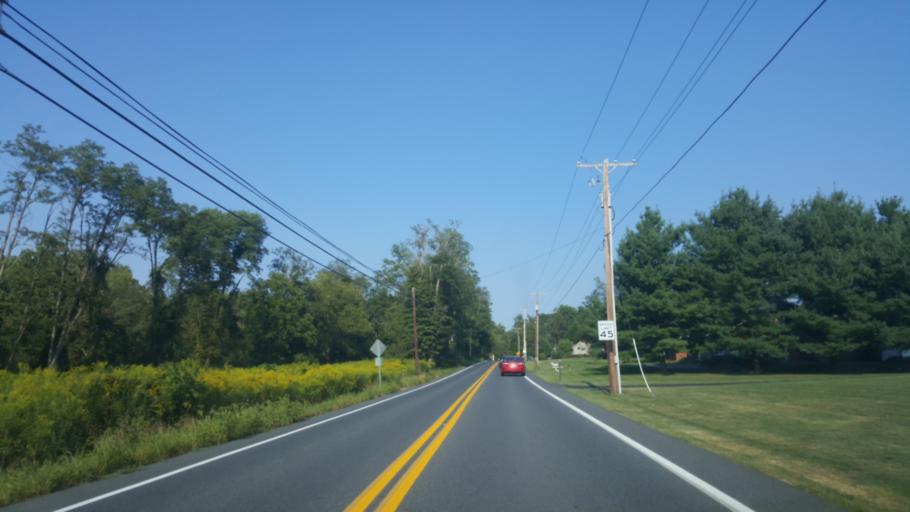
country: US
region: Pennsylvania
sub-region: Lebanon County
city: Campbelltown
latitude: 40.2391
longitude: -76.5167
